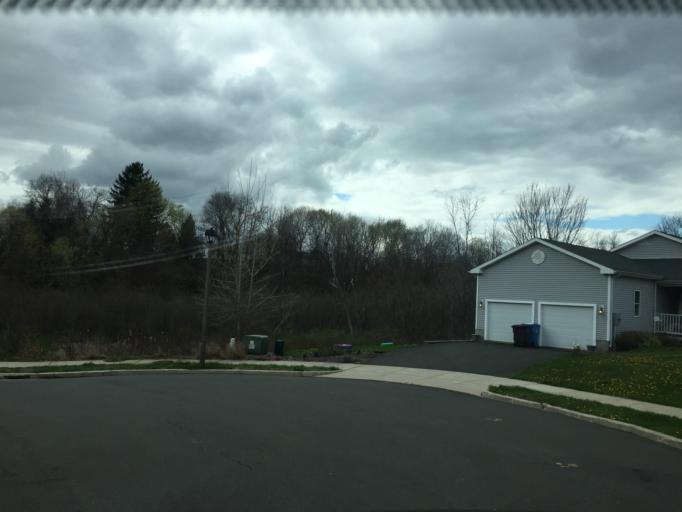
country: US
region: Connecticut
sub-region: Hartford County
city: New Britain
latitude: 41.7114
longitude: -72.7773
